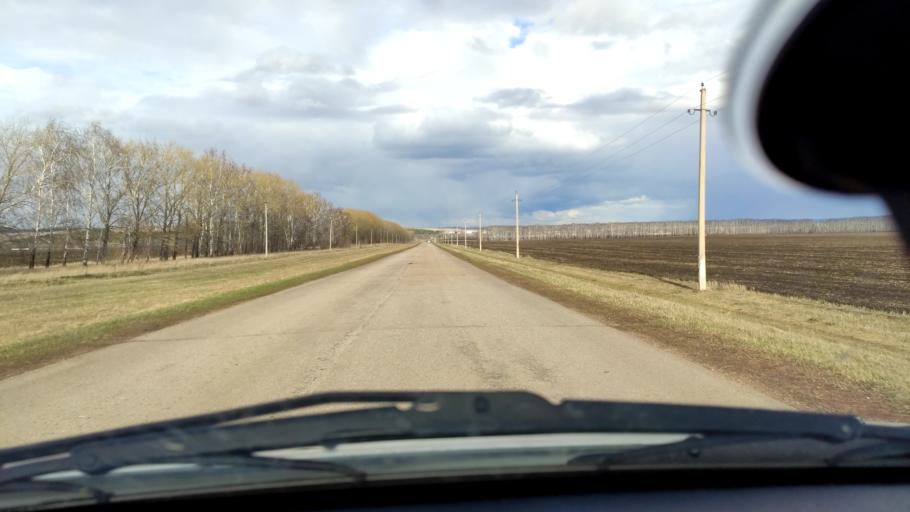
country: RU
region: Bashkortostan
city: Buzdyak
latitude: 54.7600
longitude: 54.5680
